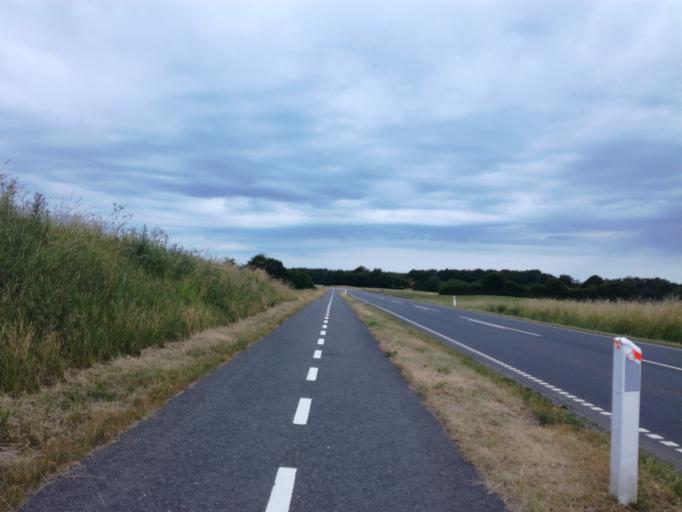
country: DK
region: South Denmark
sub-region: Vejle Kommune
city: Borkop
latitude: 55.6708
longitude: 9.6190
